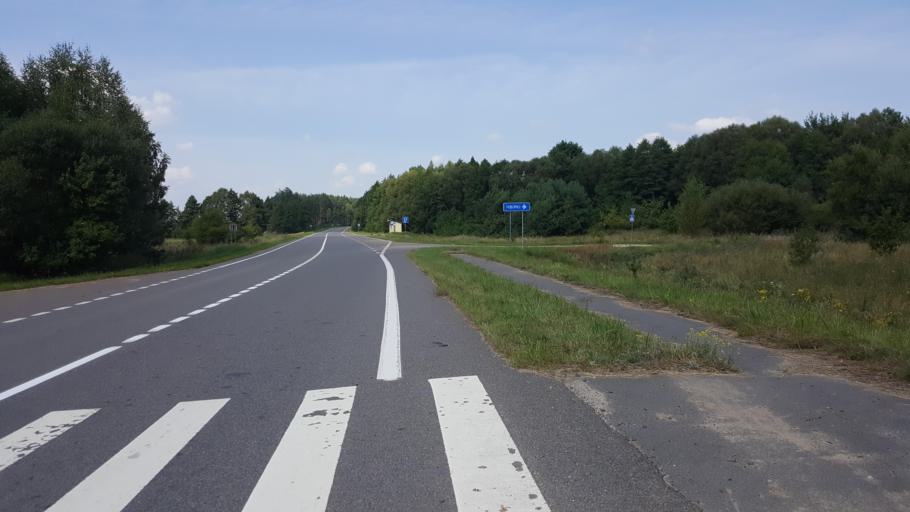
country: BY
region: Brest
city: Kamyanyuki
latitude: 52.5585
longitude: 23.6301
